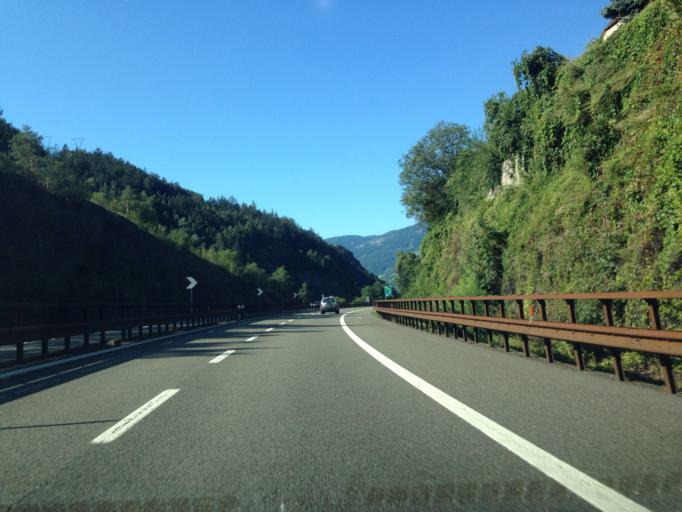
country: IT
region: Trentino-Alto Adige
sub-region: Bolzano
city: Velturno
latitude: 46.6588
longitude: 11.6063
